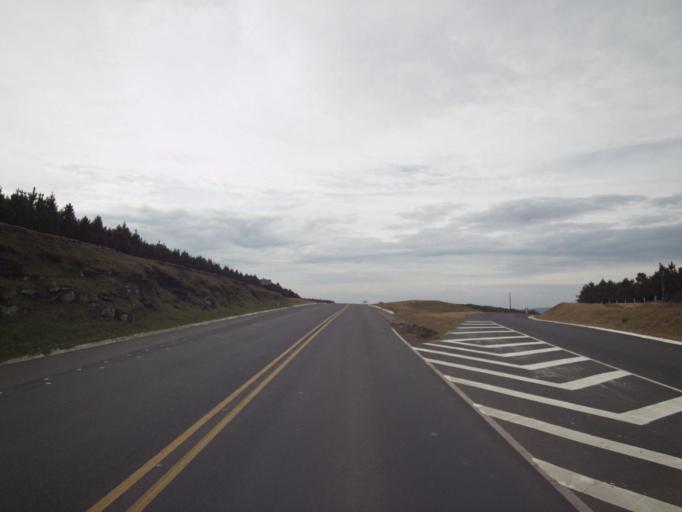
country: BR
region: Santa Catarina
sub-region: Cacador
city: Cacador
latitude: -26.6102
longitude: -51.4838
